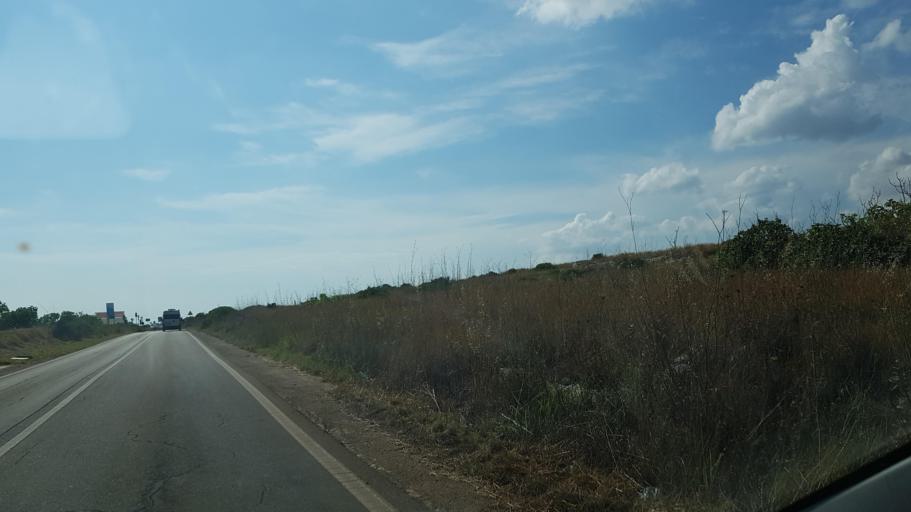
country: IT
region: Apulia
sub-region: Provincia di Lecce
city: Salve
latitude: 39.8385
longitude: 18.2338
